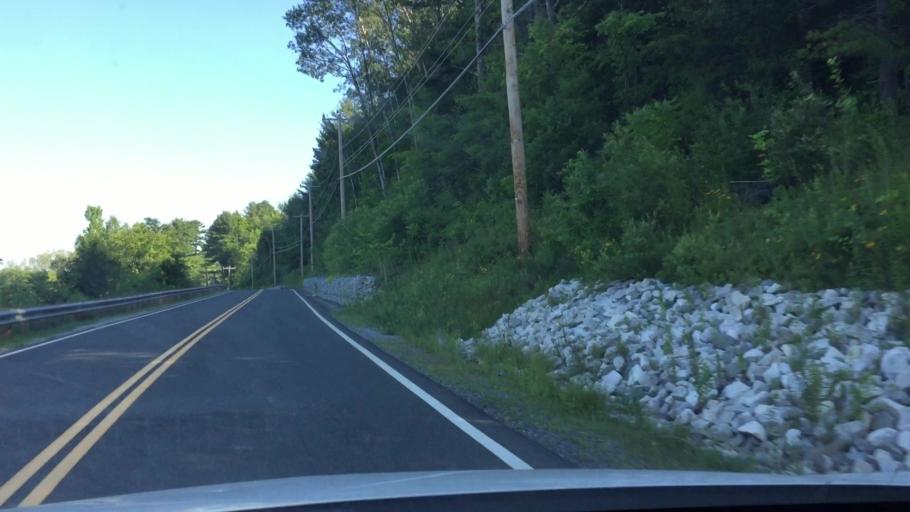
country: US
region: Massachusetts
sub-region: Berkshire County
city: Lee
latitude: 42.2714
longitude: -73.2364
